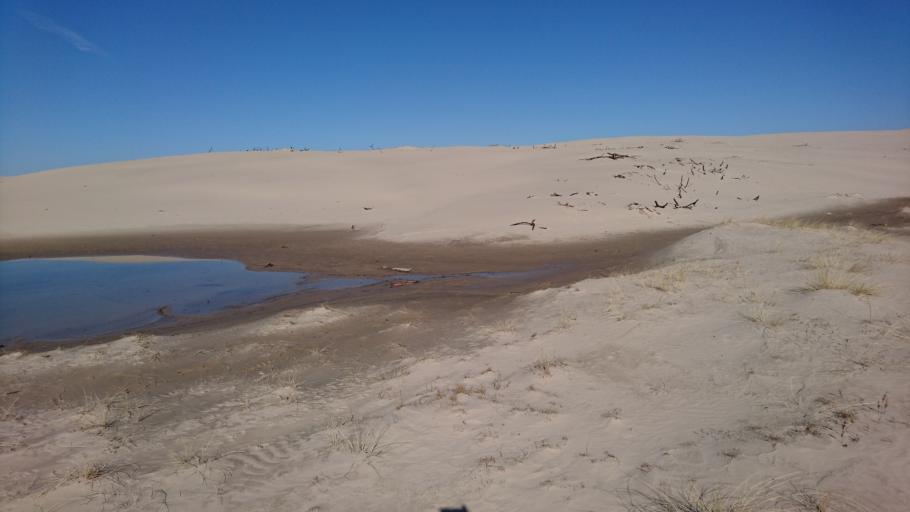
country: DK
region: North Denmark
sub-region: Frederikshavn Kommune
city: Strandby
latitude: 57.6474
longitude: 10.4047
